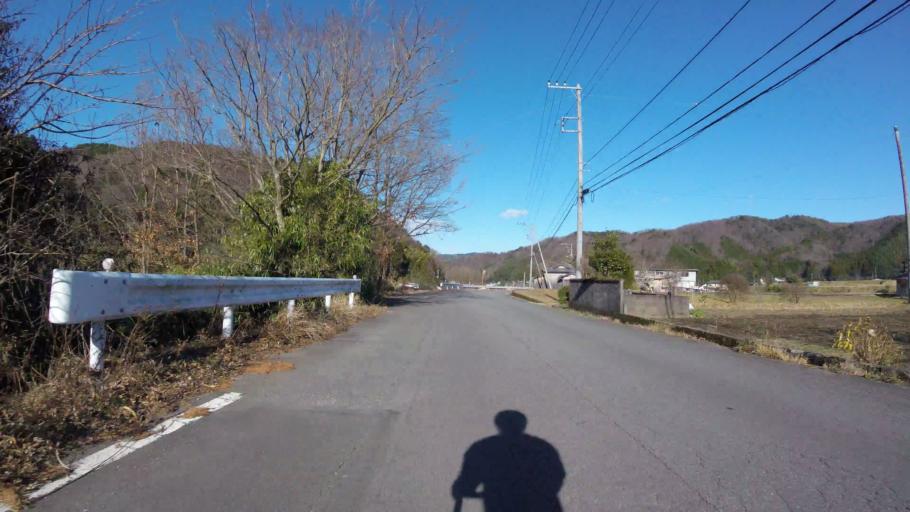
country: JP
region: Shizuoka
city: Ito
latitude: 34.9345
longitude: 138.9948
